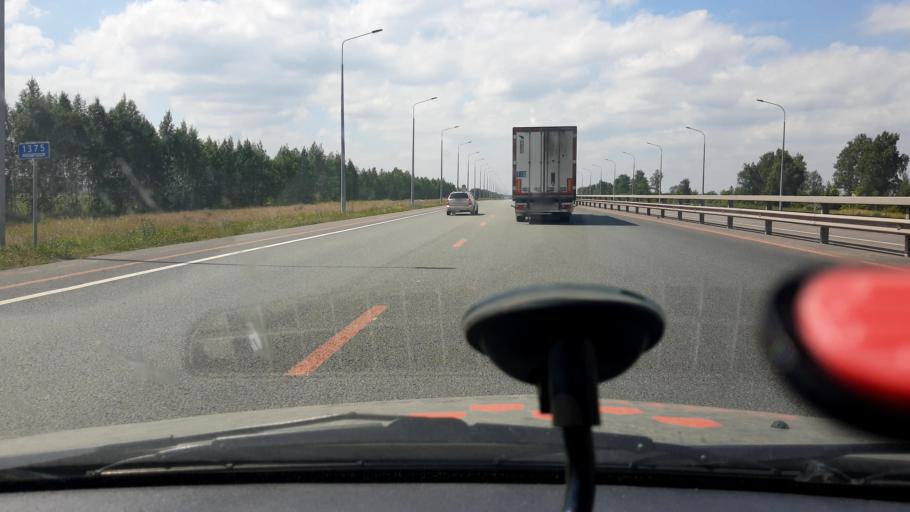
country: RU
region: Bashkortostan
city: Buzdyak
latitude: 54.6532
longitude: 54.6289
